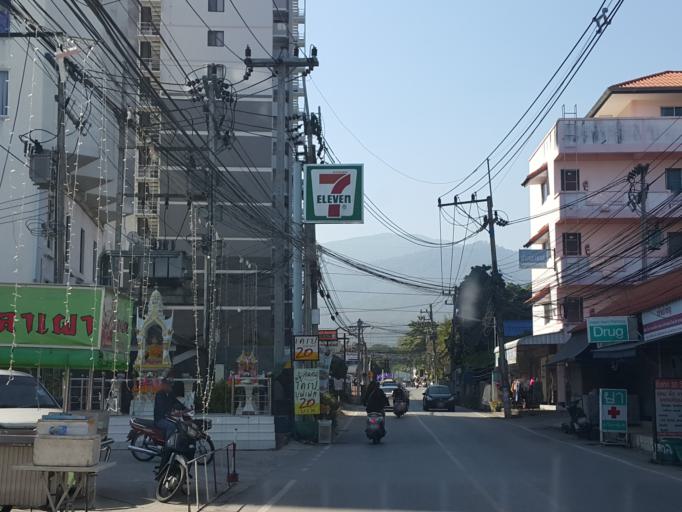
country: TH
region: Chiang Mai
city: Chiang Mai
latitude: 18.8083
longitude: 98.9642
